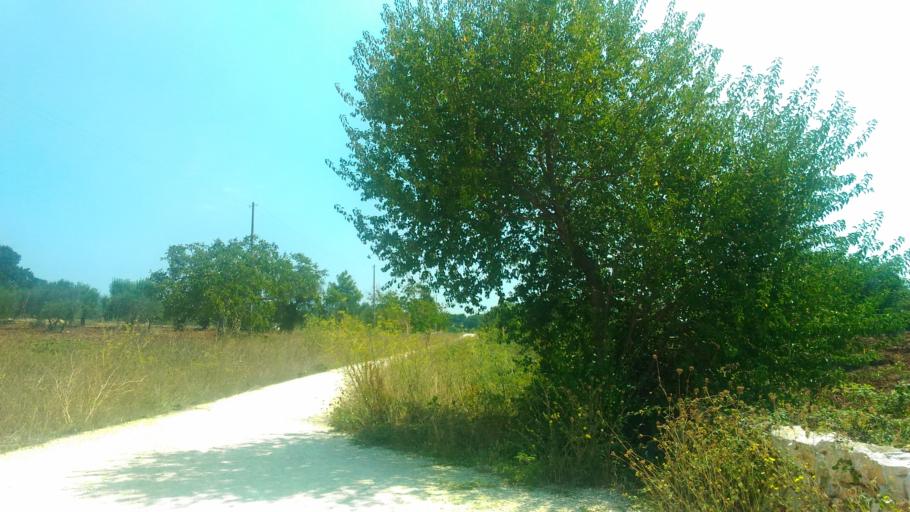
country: IT
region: Apulia
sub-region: Provincia di Brindisi
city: Cisternino
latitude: 40.7373
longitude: 17.3863
